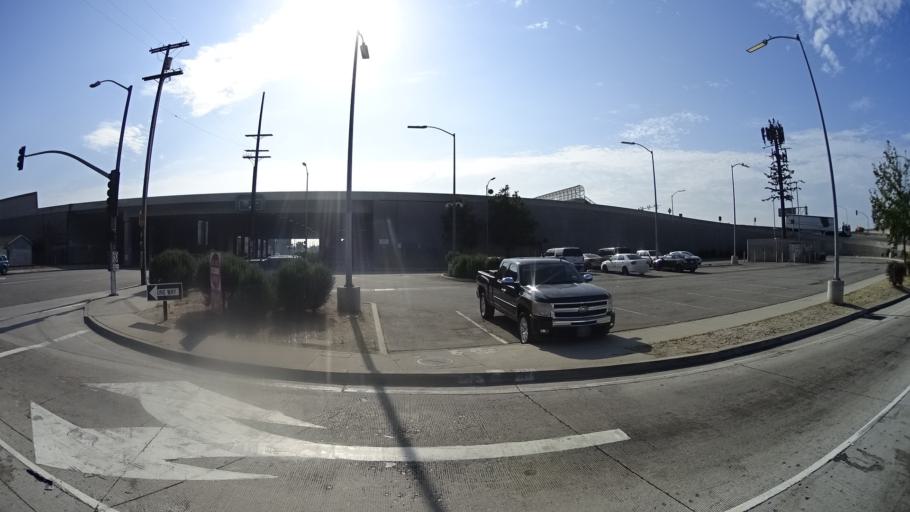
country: US
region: California
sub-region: Los Angeles County
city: Florence-Graham
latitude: 33.9888
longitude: -118.2816
